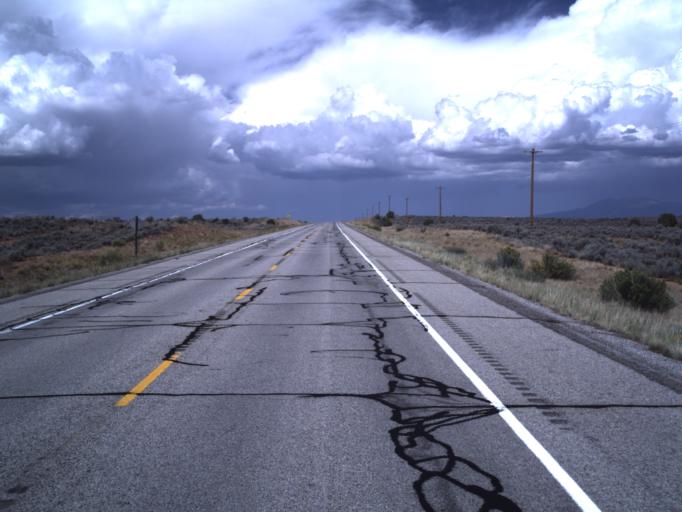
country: US
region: Utah
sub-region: San Juan County
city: Blanding
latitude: 37.4924
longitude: -109.4803
